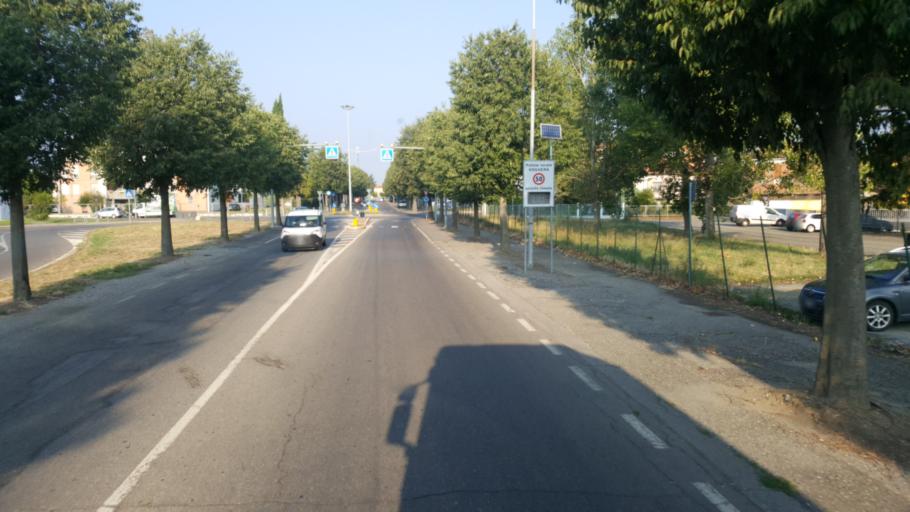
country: IT
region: Lombardy
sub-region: Provincia di Pavia
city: Voghera
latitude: 44.9865
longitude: 8.9972
